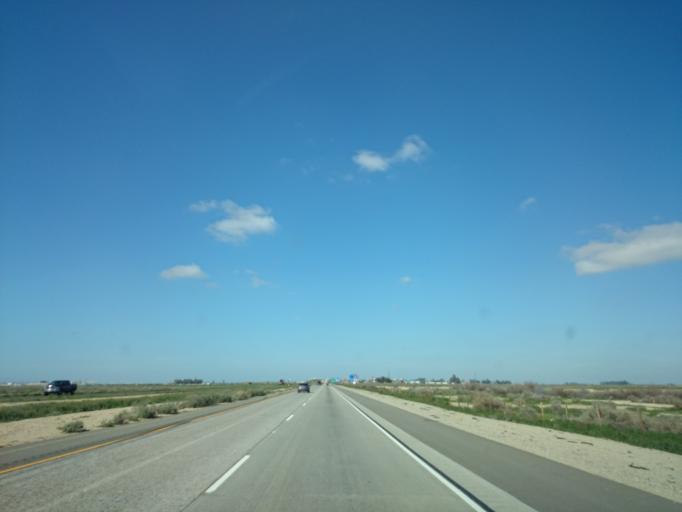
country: US
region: California
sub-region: Kern County
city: Buttonwillow
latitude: 35.3892
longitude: -119.3837
